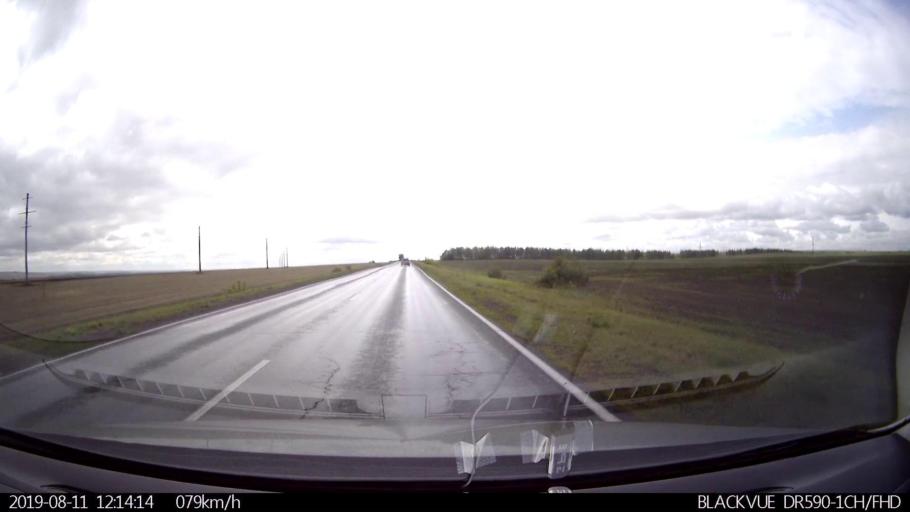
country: RU
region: Ulyanovsk
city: Ignatovka
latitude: 53.9541
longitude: 47.9827
